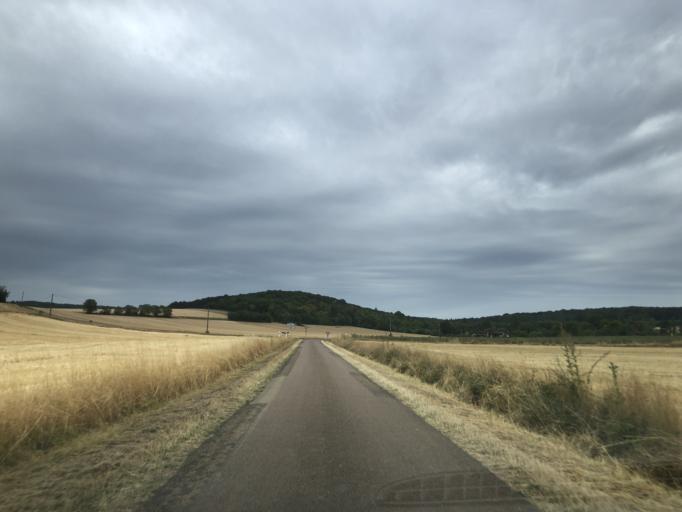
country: FR
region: Bourgogne
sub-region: Departement de l'Yonne
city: Aillant-sur-Tholon
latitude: 47.9054
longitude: 3.3353
